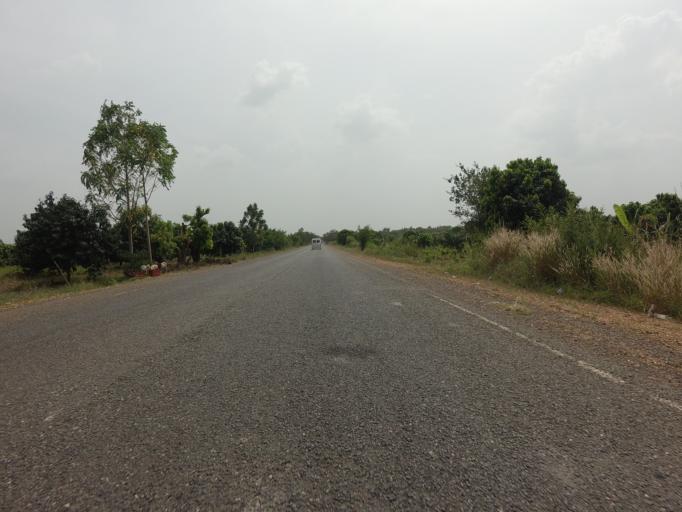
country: GH
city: Akropong
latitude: 6.0037
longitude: 0.0116
